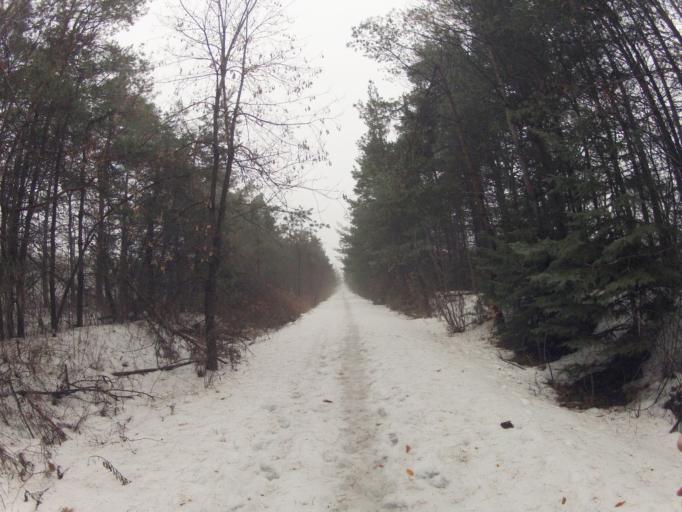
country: CA
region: Ontario
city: Brampton
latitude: 43.8382
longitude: -79.8895
